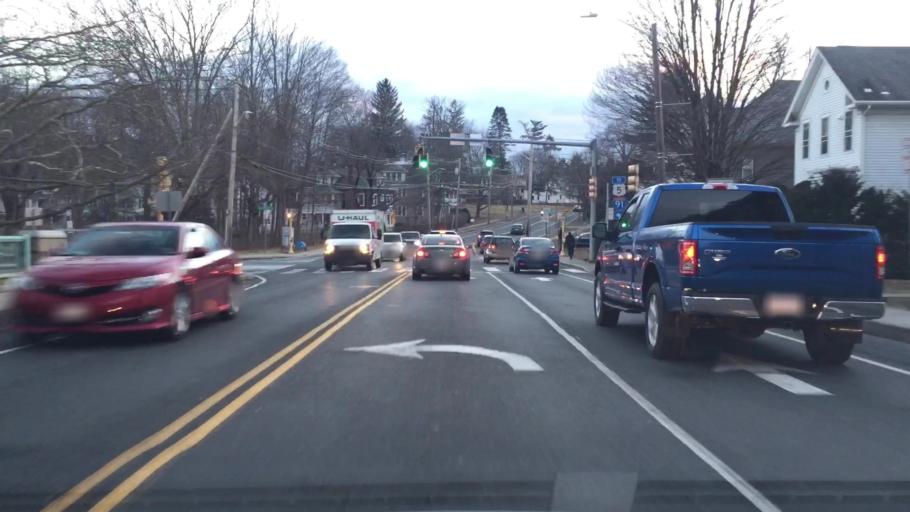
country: US
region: Massachusetts
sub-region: Hampshire County
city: Northampton
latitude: 42.3153
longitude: -72.6334
